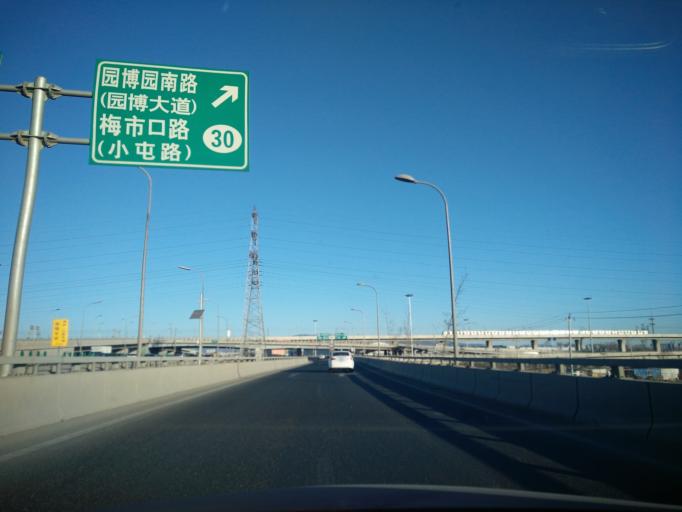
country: CN
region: Beijing
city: Lugu
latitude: 39.8615
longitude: 116.2104
